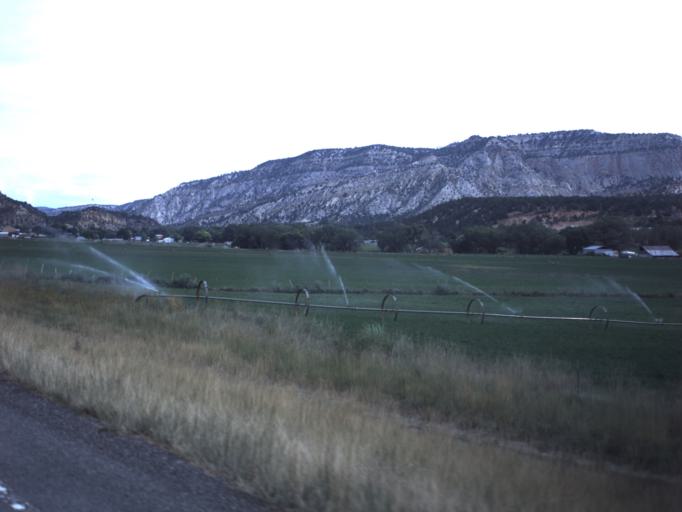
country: US
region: Utah
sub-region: Kane County
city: Kanab
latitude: 37.2664
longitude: -112.6528
